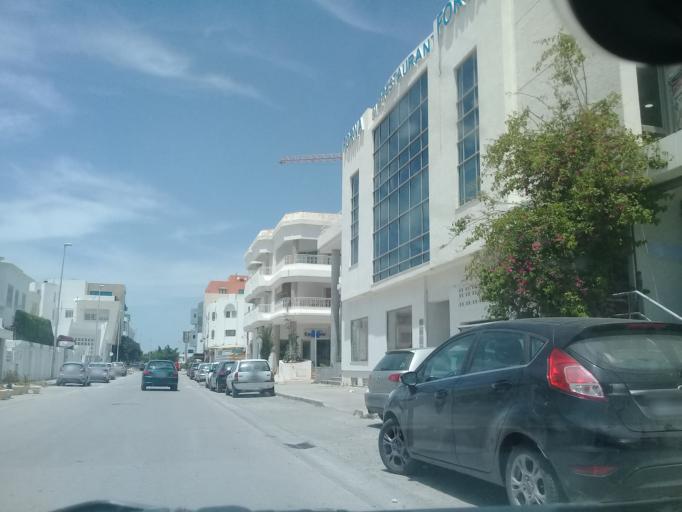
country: TN
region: Ariana
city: Ariana
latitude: 36.8343
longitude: 10.2302
